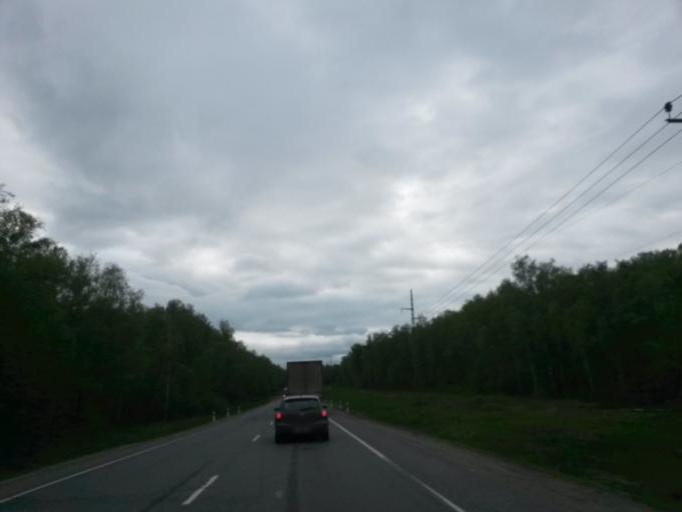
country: RU
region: Moskovskaya
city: Klimovsk
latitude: 55.3314
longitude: 37.6489
